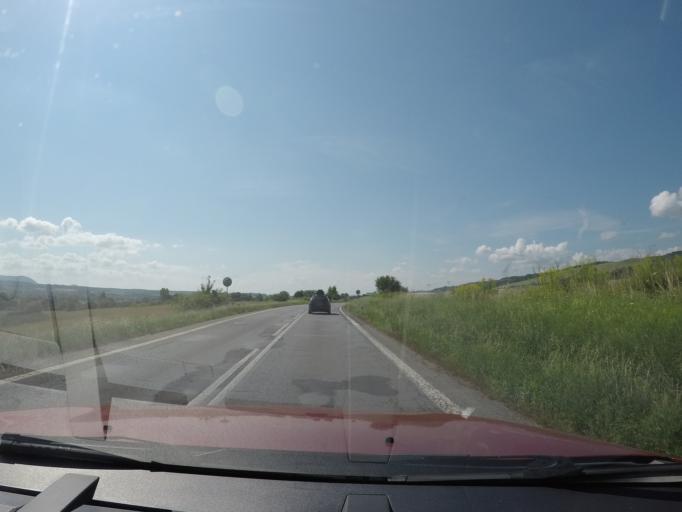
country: SK
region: Presovsky
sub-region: Okres Presov
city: Presov
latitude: 48.9385
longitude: 21.2399
